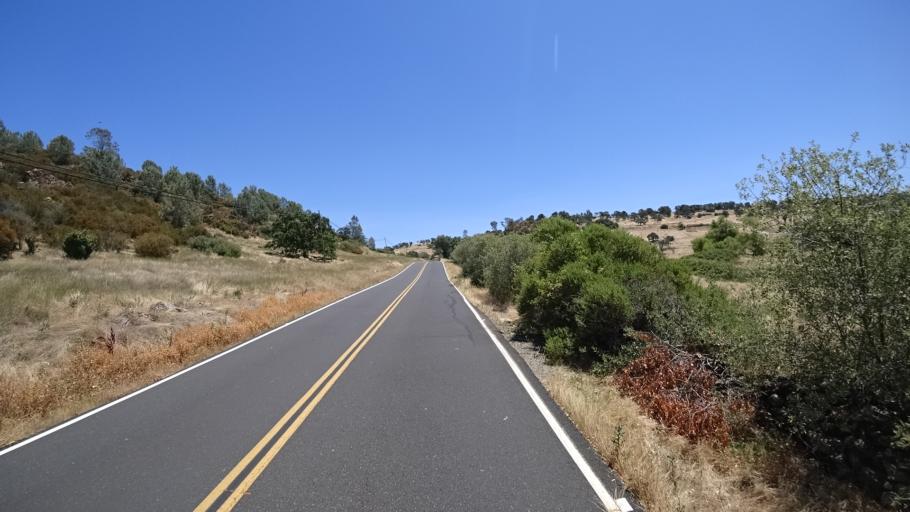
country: US
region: California
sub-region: Calaveras County
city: Valley Springs
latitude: 38.2323
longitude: -120.8043
